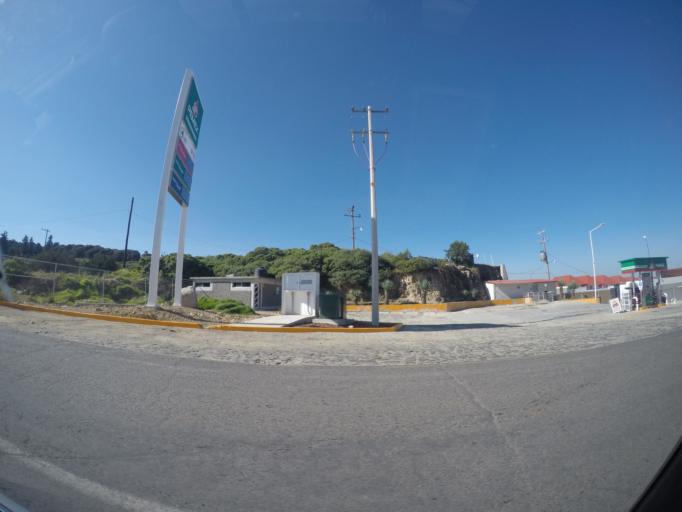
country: MX
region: Hidalgo
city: Mineral del Monte
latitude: 20.1402
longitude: -98.6902
